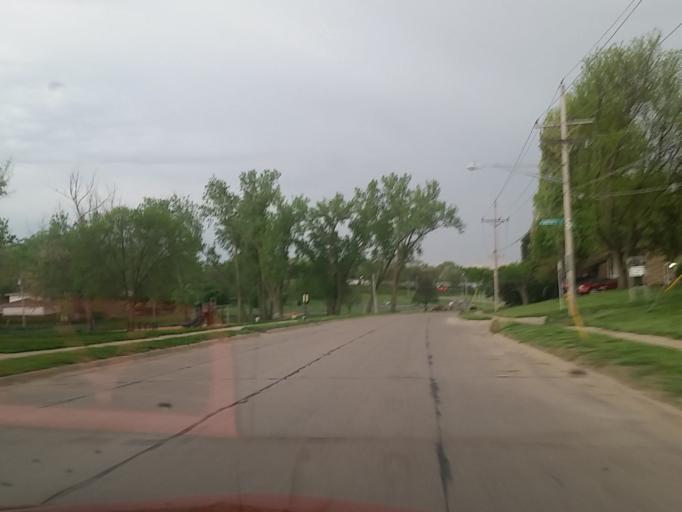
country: US
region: Nebraska
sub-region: Sarpy County
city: Offutt Air Force Base
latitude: 41.1442
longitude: -95.9214
